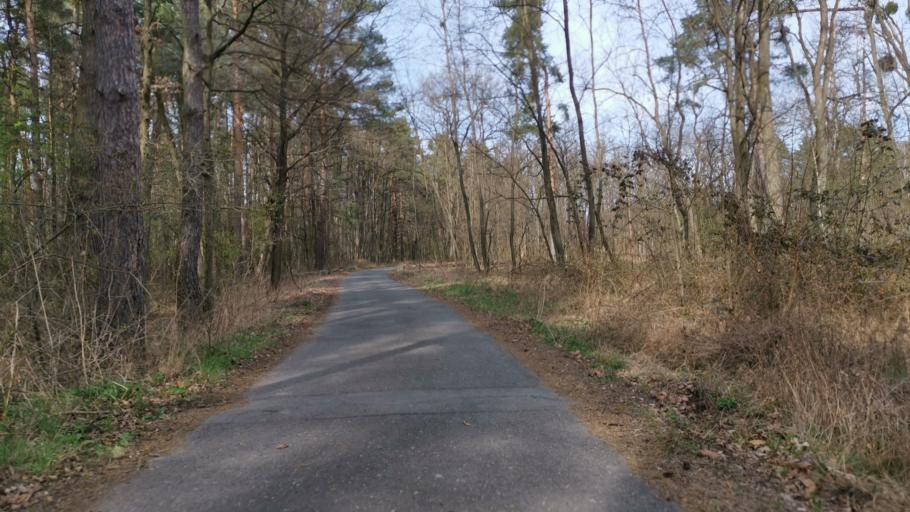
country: SK
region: Trnavsky
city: Gbely
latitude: 48.6742
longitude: 17.0556
